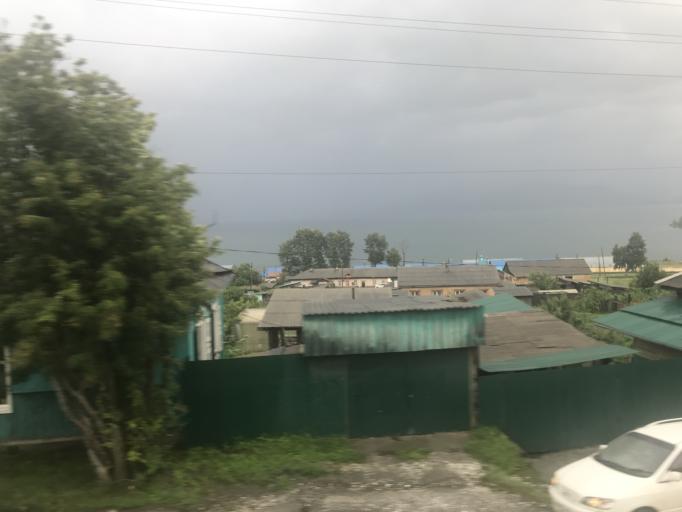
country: RU
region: Irkutsk
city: Kultuk
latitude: 51.7311
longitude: 103.7212
